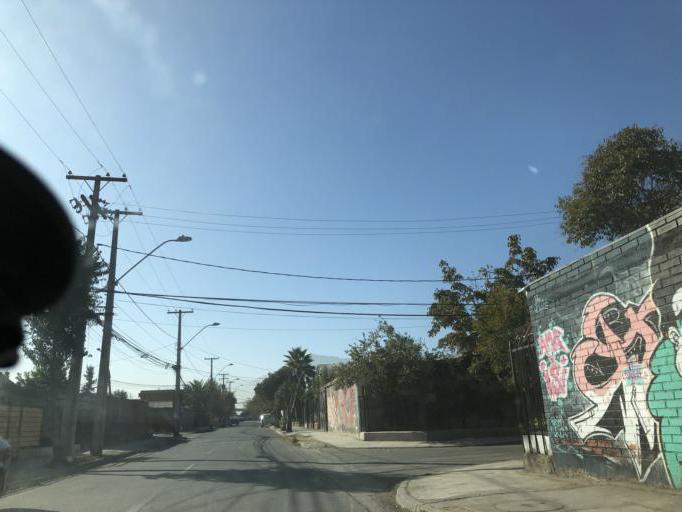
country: CL
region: Santiago Metropolitan
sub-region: Provincia de Cordillera
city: Puente Alto
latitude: -33.6287
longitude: -70.5917
